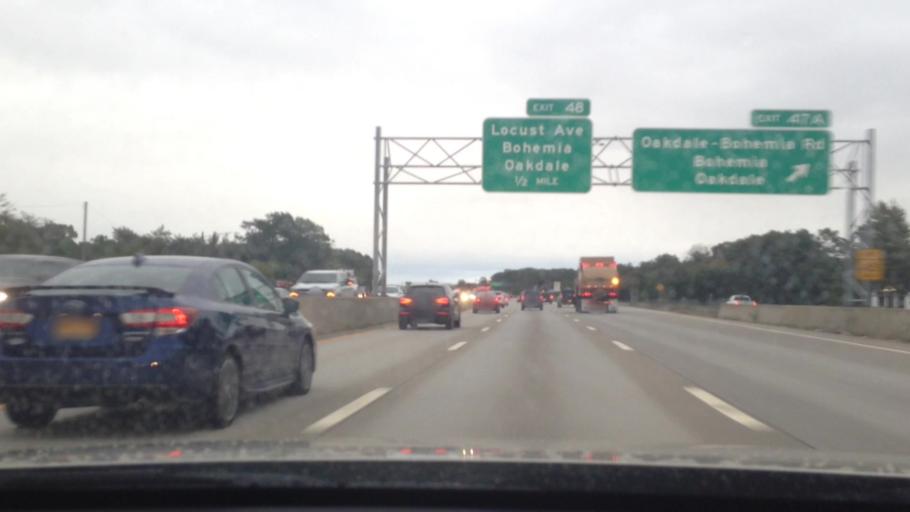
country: US
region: New York
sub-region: Suffolk County
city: Oakdale
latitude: 40.7491
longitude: -73.1359
